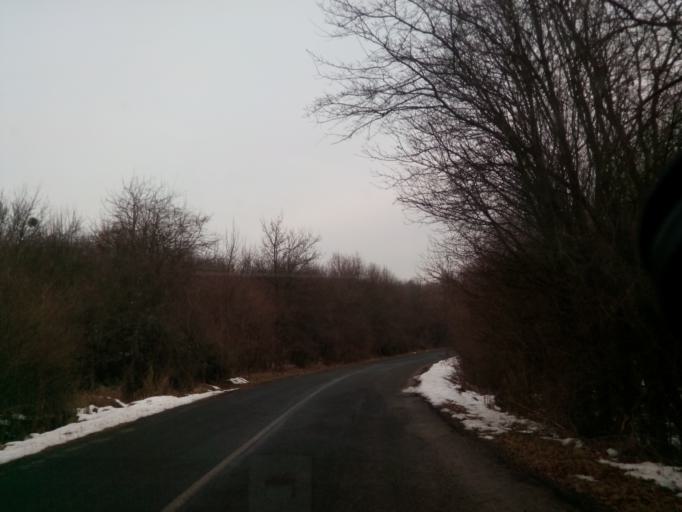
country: HU
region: Borsod-Abauj-Zemplen
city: Gonc
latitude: 48.4835
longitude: 21.3922
